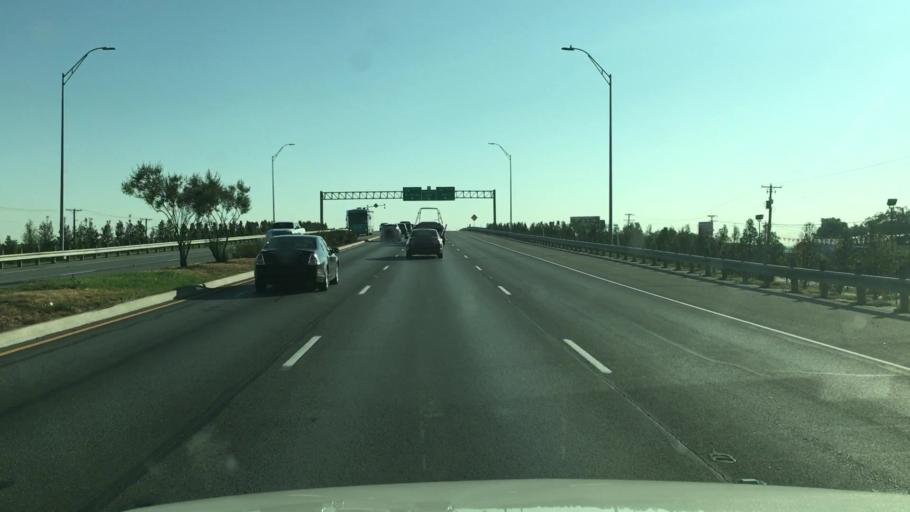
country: US
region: Texas
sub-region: Johnson County
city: Burleson
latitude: 32.5484
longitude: -97.3237
